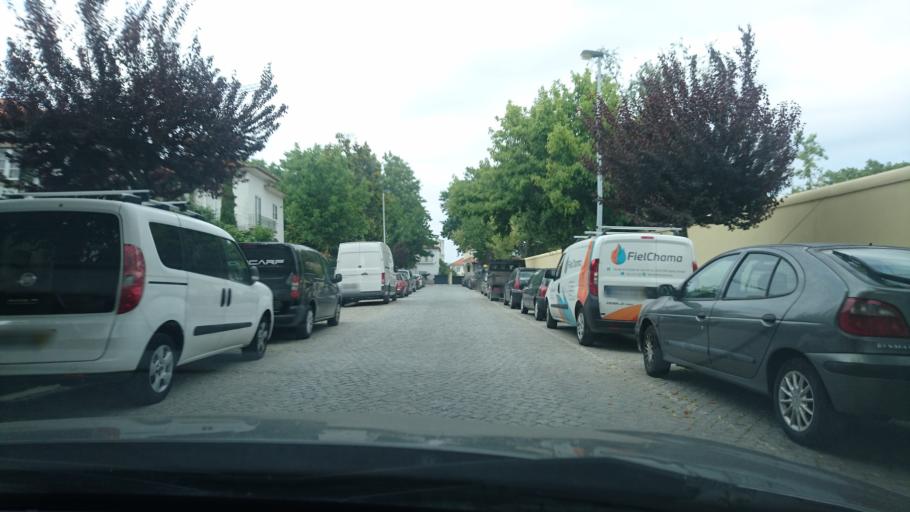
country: PT
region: Porto
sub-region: Porto
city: Porto
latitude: 41.1639
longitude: -8.5936
